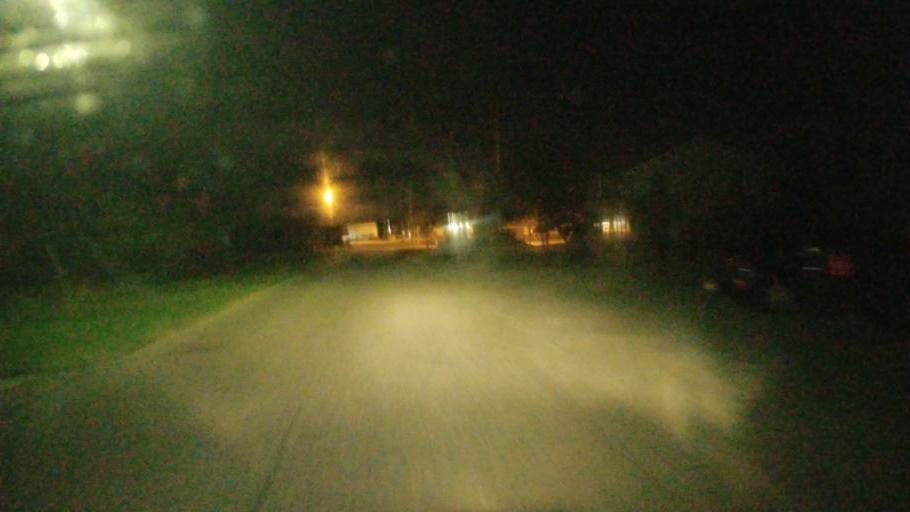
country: US
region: North Carolina
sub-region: Dare County
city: Kill Devil Hills
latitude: 35.9978
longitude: -75.6491
